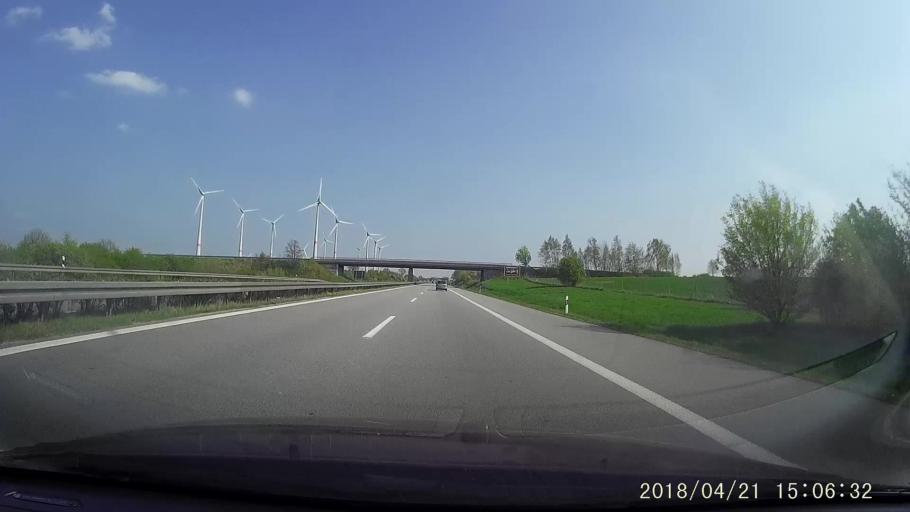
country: DE
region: Saxony
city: Kodersdorf
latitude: 51.2122
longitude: 14.9379
